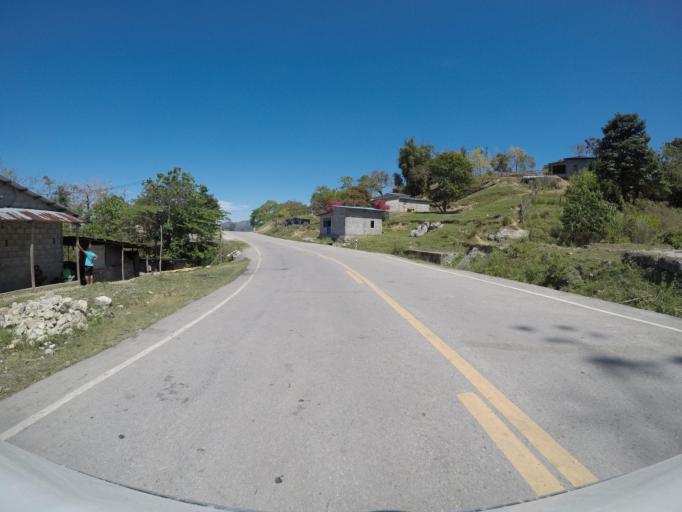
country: TL
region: Manatuto
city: Manatuto
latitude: -8.8252
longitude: 125.9841
